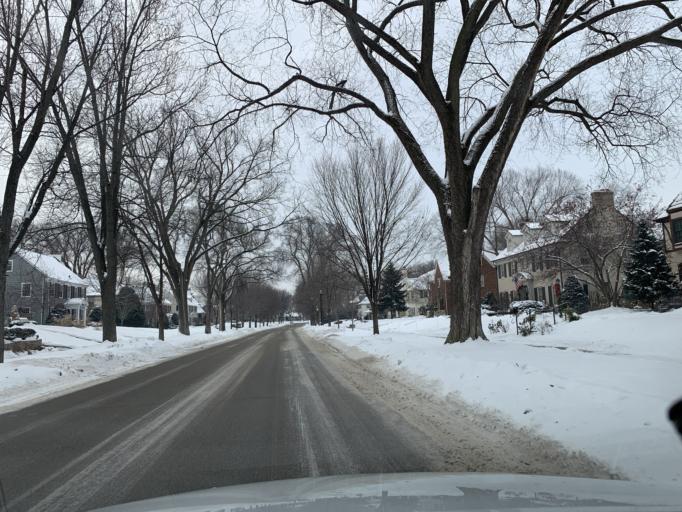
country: US
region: Minnesota
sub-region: Hennepin County
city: Edina
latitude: 44.9164
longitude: -93.3413
